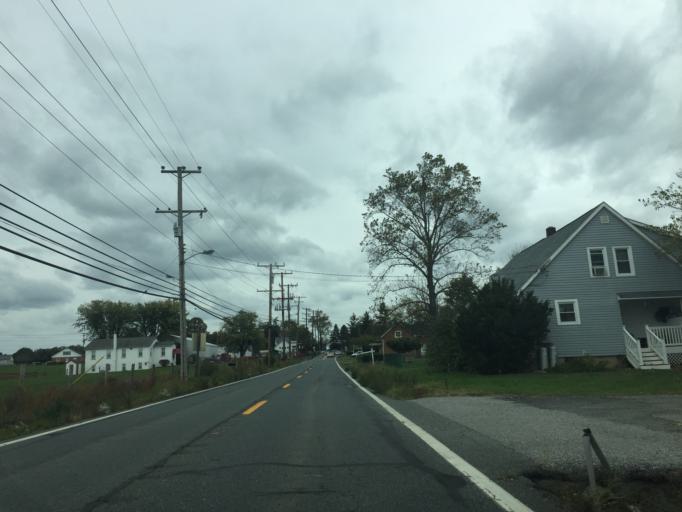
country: US
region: Maryland
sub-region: Harford County
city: Riverside
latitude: 39.5562
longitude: -76.2527
